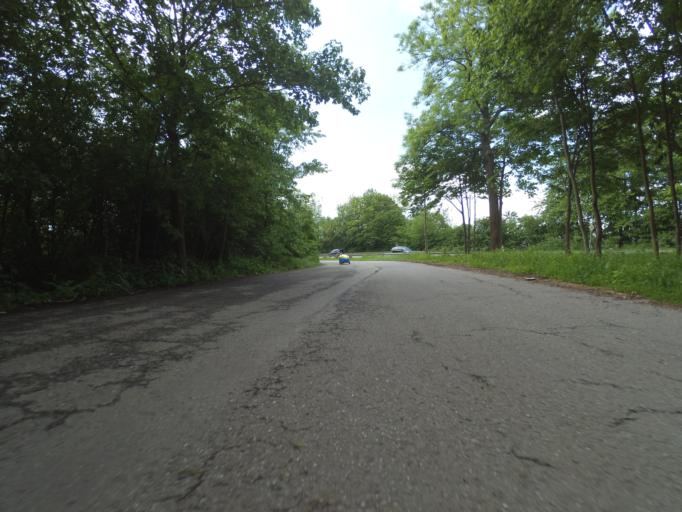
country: DE
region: Lower Saxony
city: Algermissen
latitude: 52.2312
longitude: 9.9892
